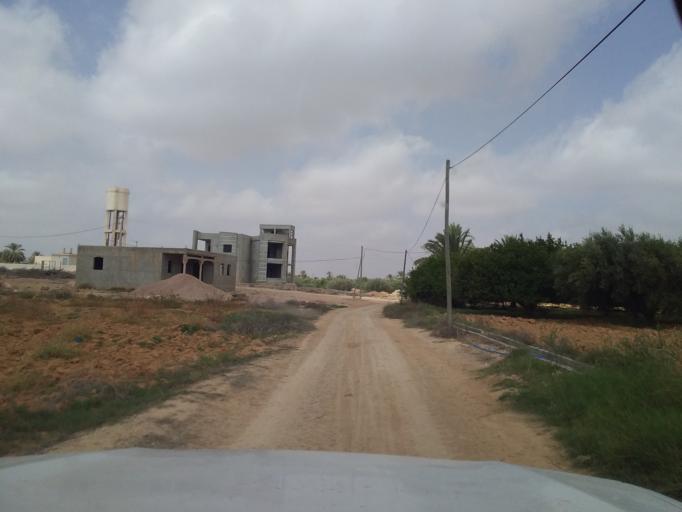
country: TN
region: Madanin
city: Medenine
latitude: 33.6233
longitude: 10.3133
